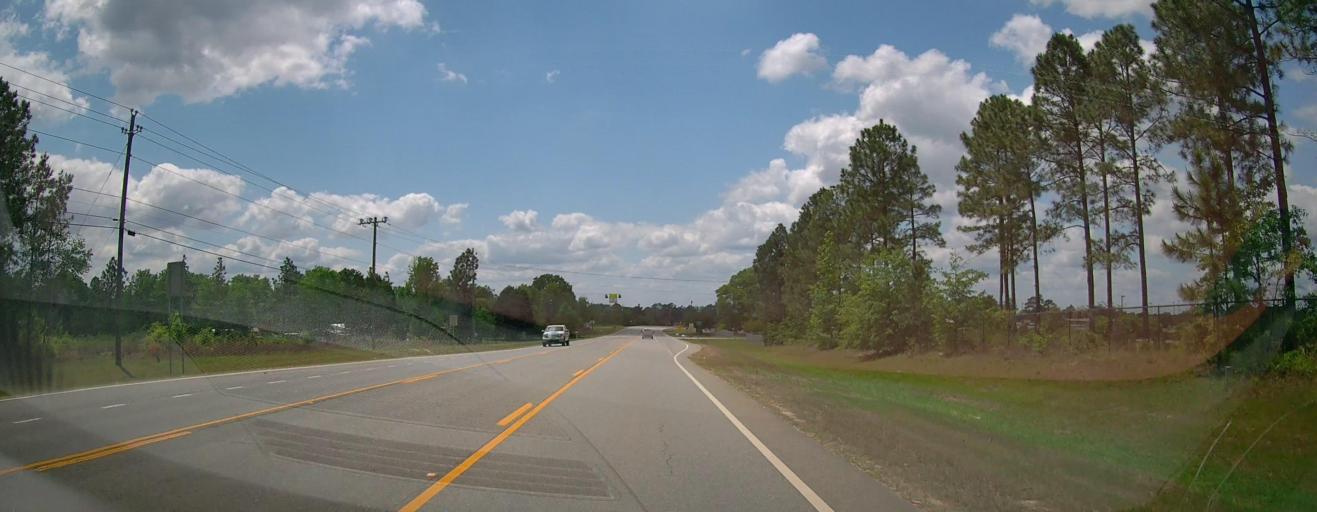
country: US
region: Georgia
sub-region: Laurens County
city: East Dublin
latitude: 32.5624
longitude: -82.8138
